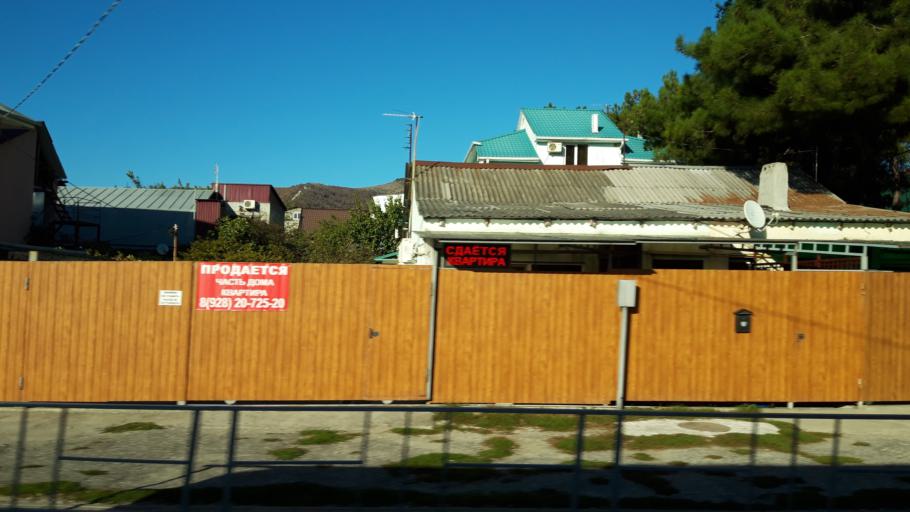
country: RU
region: Krasnodarskiy
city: Kabardinka
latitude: 44.6493
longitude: 37.9460
